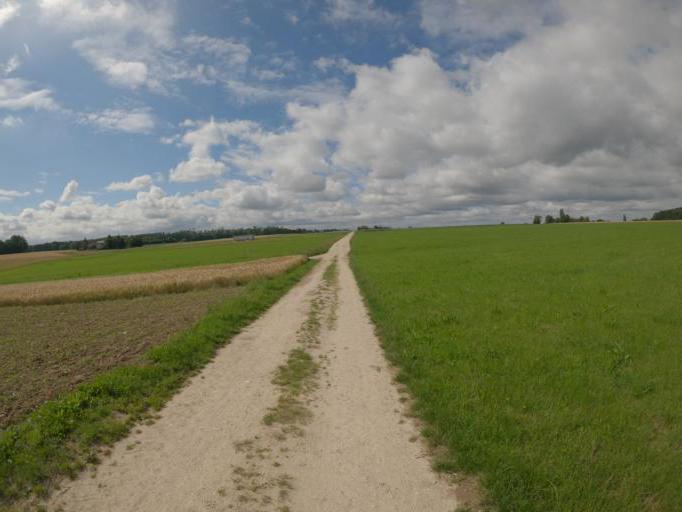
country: DE
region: Baden-Wuerttemberg
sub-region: Regierungsbezirk Stuttgart
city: Ebersbach an der Fils
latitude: 48.7000
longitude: 9.5174
